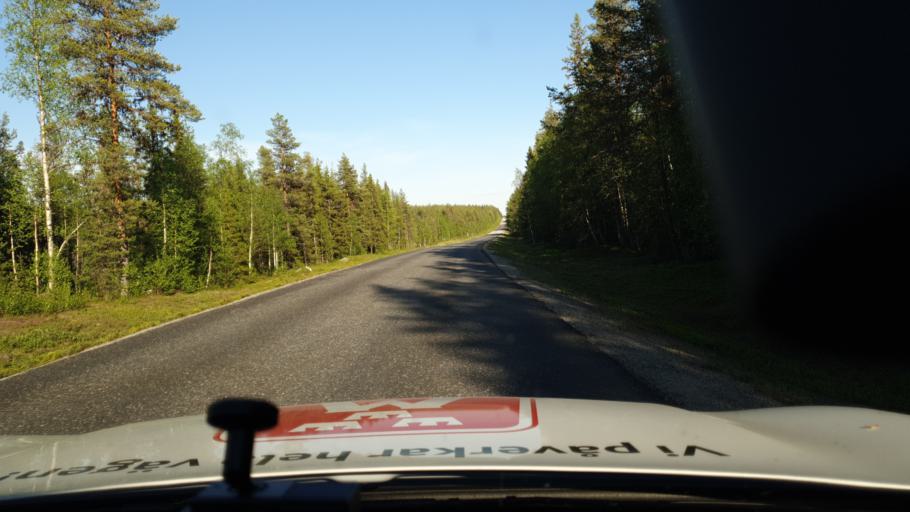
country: SE
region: Vaesterbotten
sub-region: Lycksele Kommun
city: Soderfors
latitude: 64.6908
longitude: 17.7748
